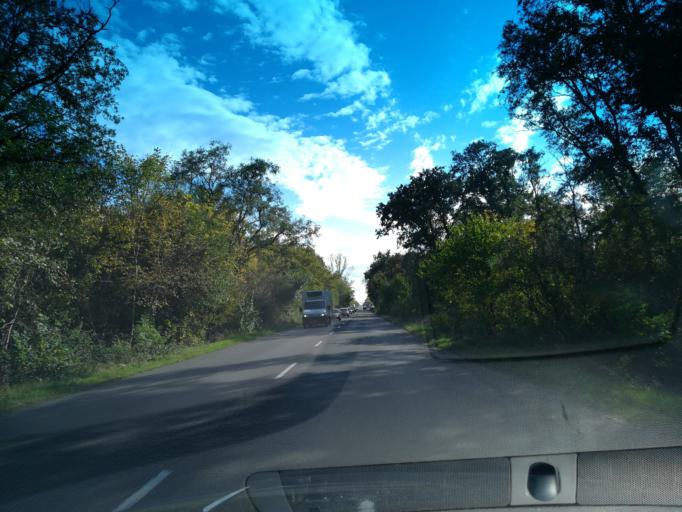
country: BG
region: Stara Zagora
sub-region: Obshtina Stara Zagora
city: Stara Zagora
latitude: 42.3526
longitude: 25.6582
